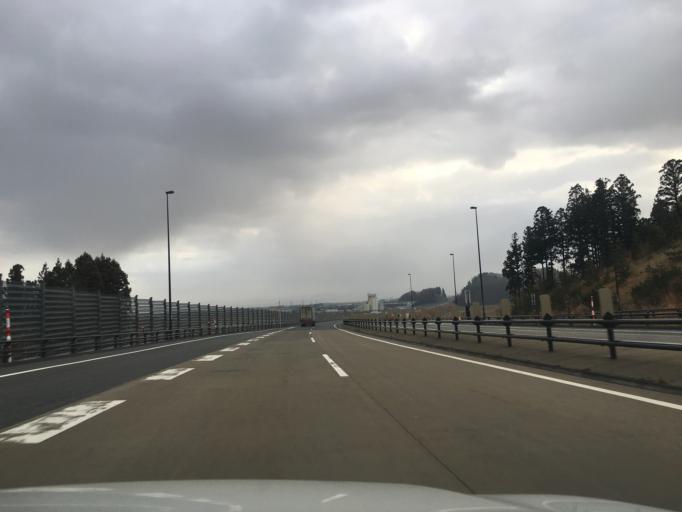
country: JP
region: Yamagata
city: Tsuruoka
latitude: 38.7035
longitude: 139.7219
